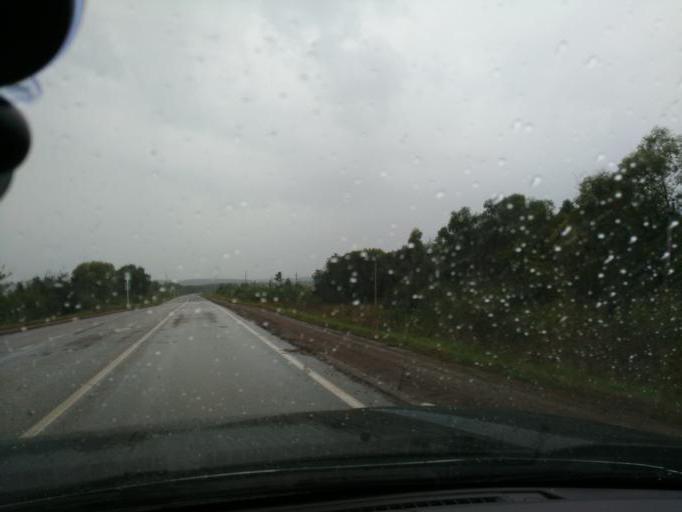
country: RU
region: Perm
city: Barda
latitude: 56.9438
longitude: 55.6131
